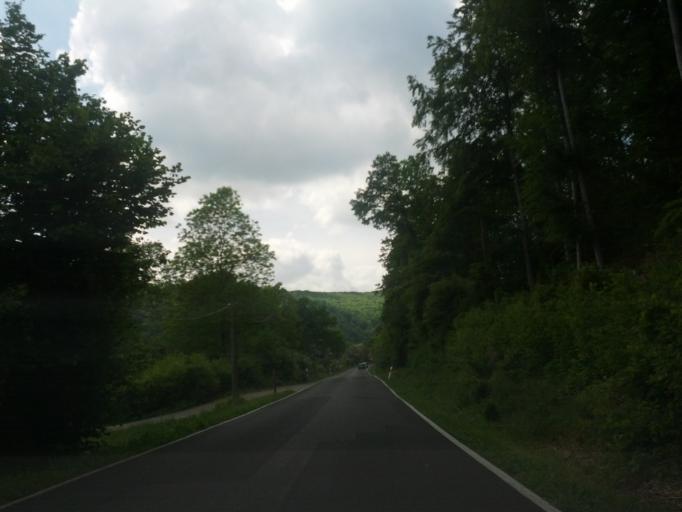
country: DE
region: Thuringia
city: Frankenroda
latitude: 51.0920
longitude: 10.2902
